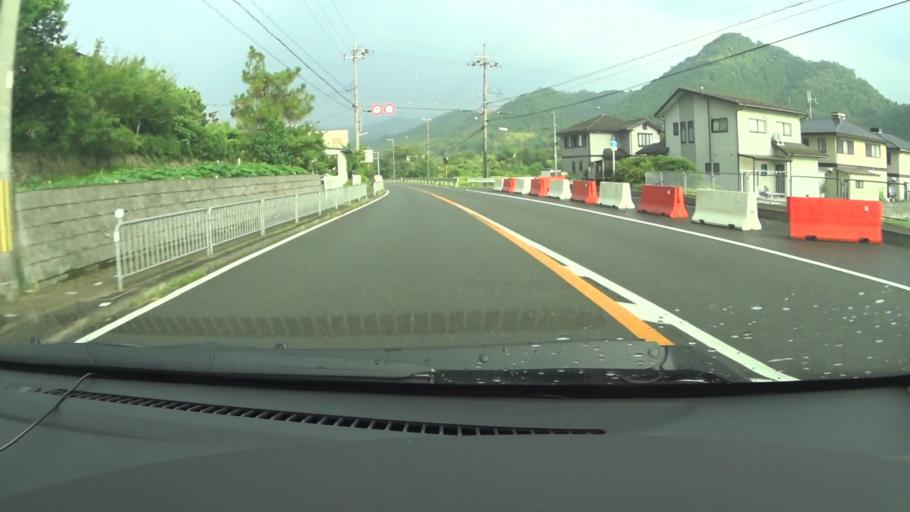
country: JP
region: Kyoto
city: Ayabe
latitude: 35.2927
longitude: 135.2694
